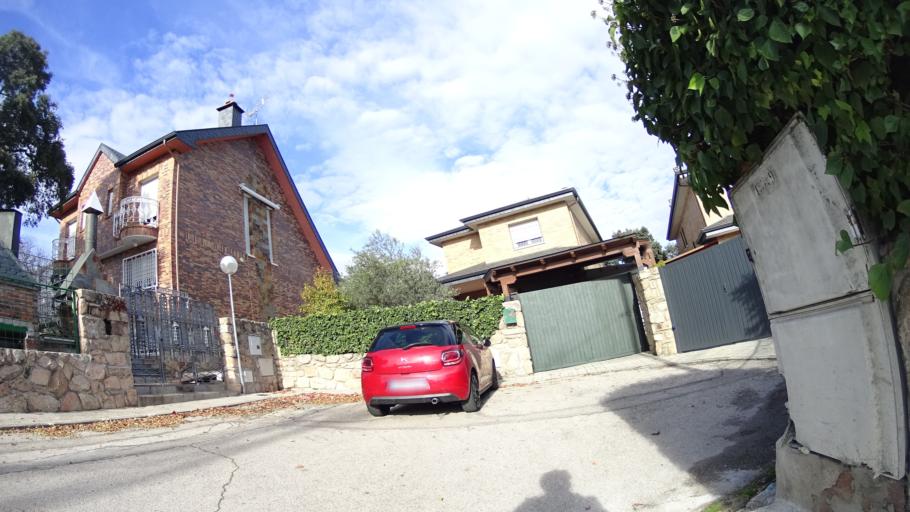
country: ES
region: Madrid
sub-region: Provincia de Madrid
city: Galapagar
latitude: 40.5807
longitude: -4.0172
